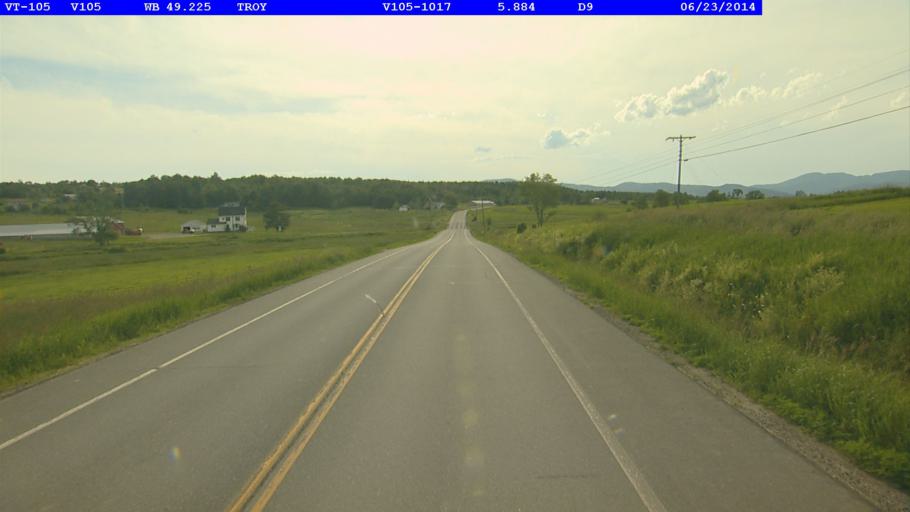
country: US
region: Vermont
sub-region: Orleans County
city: Newport
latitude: 44.9799
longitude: -72.3445
